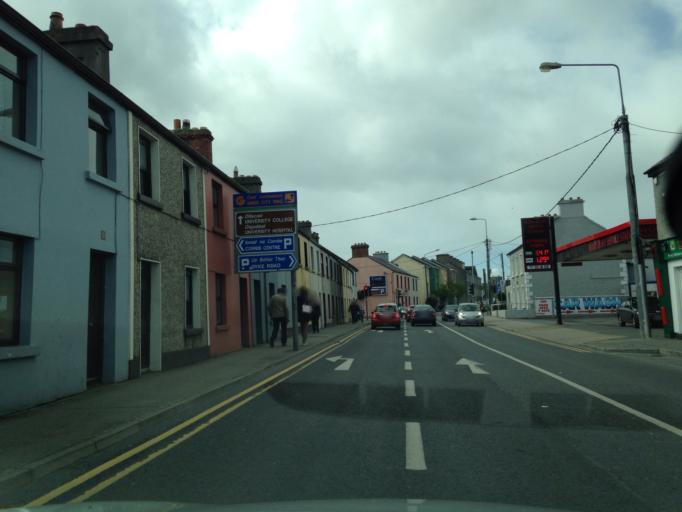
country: IE
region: Connaught
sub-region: County Galway
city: Gaillimh
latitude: 53.2779
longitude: -9.0507
